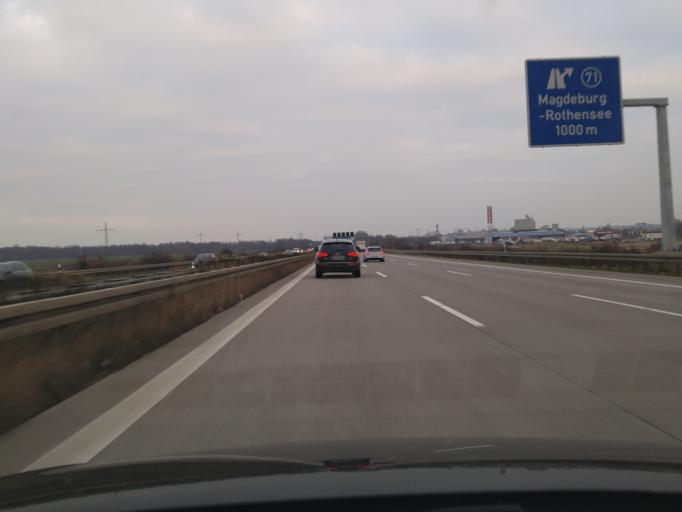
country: DE
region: Saxony-Anhalt
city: Barleben
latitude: 52.2027
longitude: 11.6501
